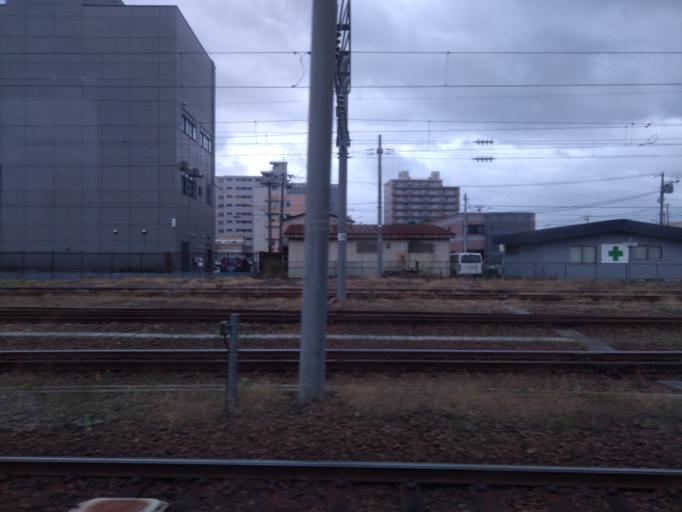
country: JP
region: Hokkaido
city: Hakodate
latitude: 41.7773
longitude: 140.7283
